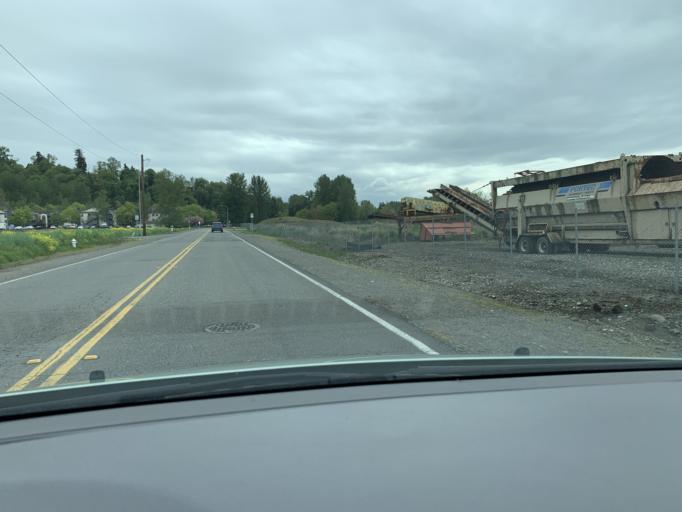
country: US
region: Washington
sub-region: King County
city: Kent
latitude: 47.3963
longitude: -122.2233
